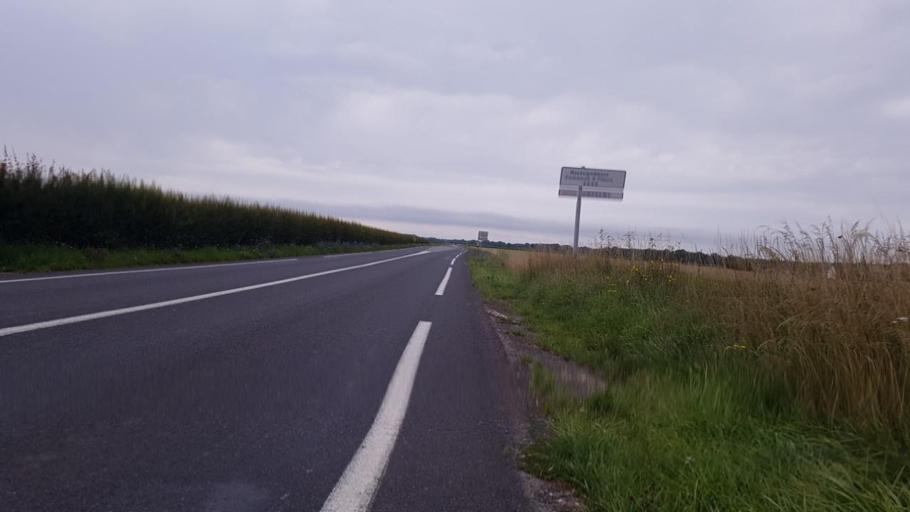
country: FR
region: Champagne-Ardenne
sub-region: Departement de la Marne
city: Pargny-sur-Saulx
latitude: 48.7585
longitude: 4.7551
